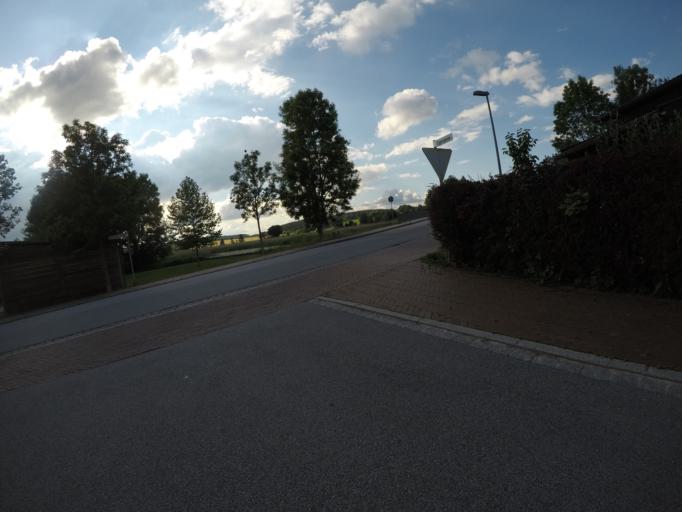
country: DE
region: Bavaria
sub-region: Lower Bavaria
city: Frontenhausen
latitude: 48.5486
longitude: 12.5260
